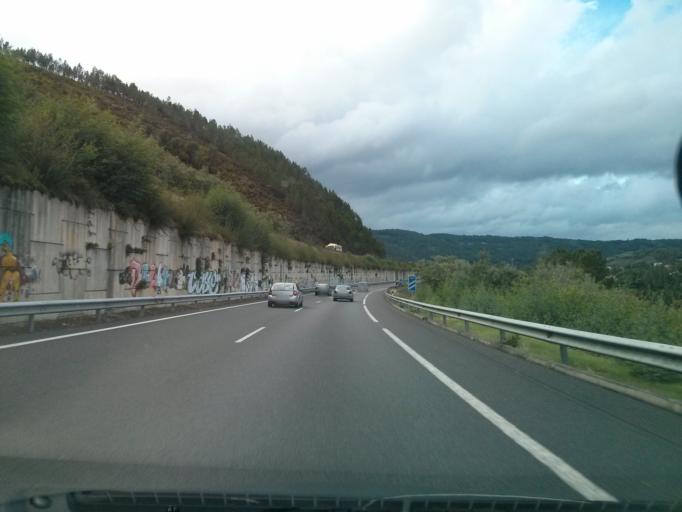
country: ES
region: Galicia
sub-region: Provincia de Ourense
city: Toen
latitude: 42.3361
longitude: -7.9851
